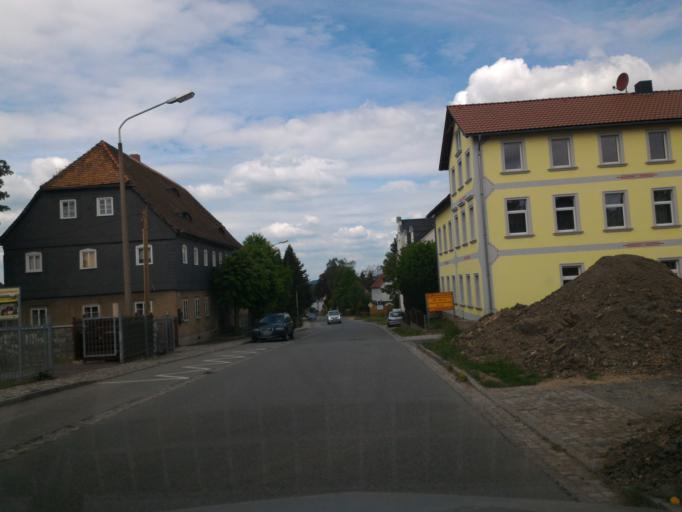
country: DE
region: Saxony
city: Neugersdorf
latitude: 50.9814
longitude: 14.6064
